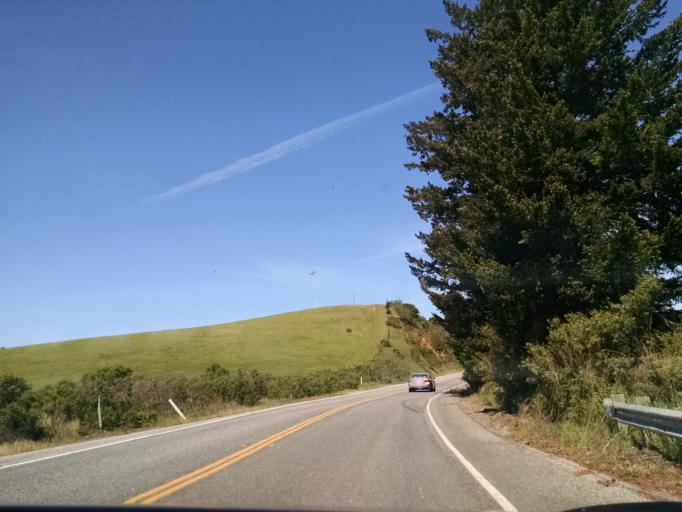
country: US
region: California
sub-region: San Mateo County
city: Portola Valley
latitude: 37.3516
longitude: -122.2398
